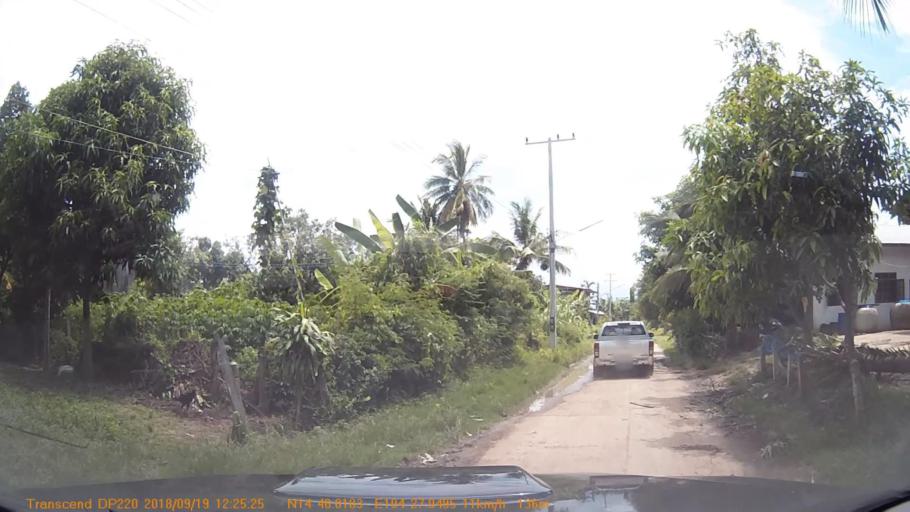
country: TH
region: Sisaket
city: Khun Han
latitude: 14.6666
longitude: 104.4512
